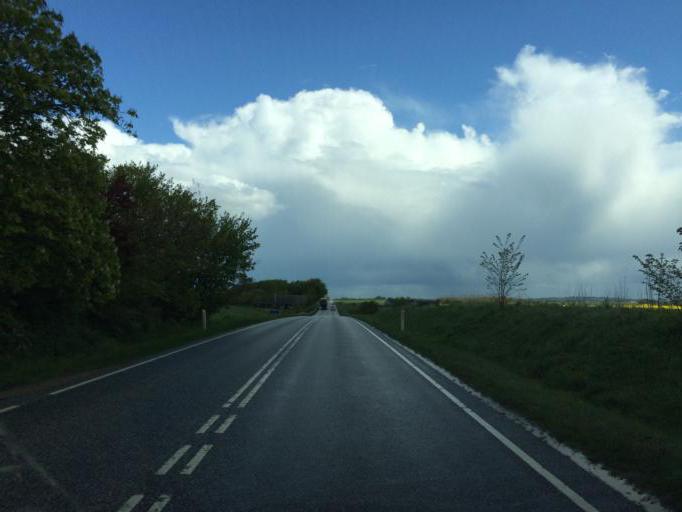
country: DK
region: Central Jutland
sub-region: Holstebro Kommune
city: Holstebro
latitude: 56.4035
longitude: 8.6787
